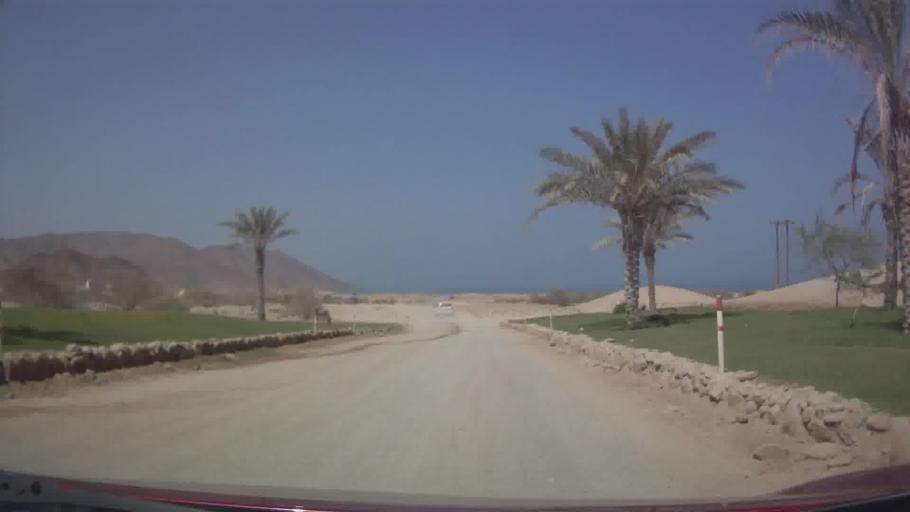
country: OM
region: Muhafazat Masqat
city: Muscat
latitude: 23.4153
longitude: 58.7853
